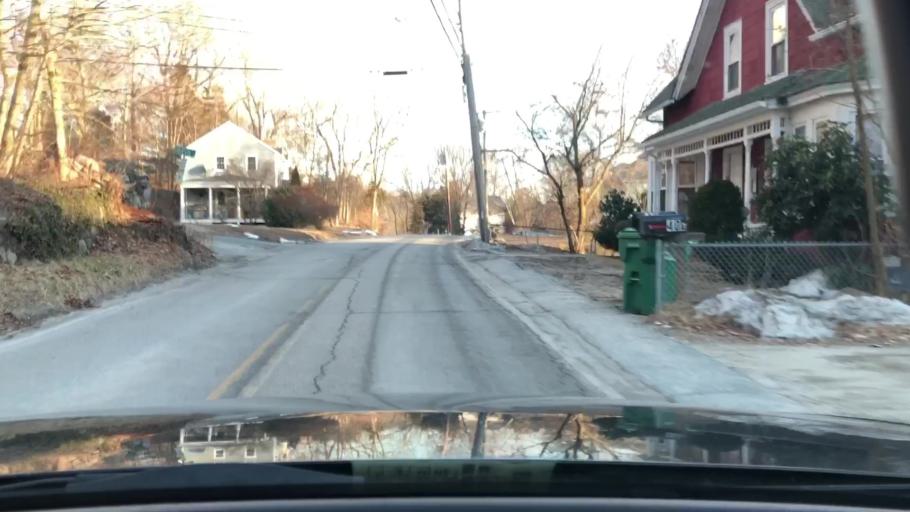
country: US
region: Massachusetts
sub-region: Worcester County
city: Millville
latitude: 42.0278
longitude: -71.5765
